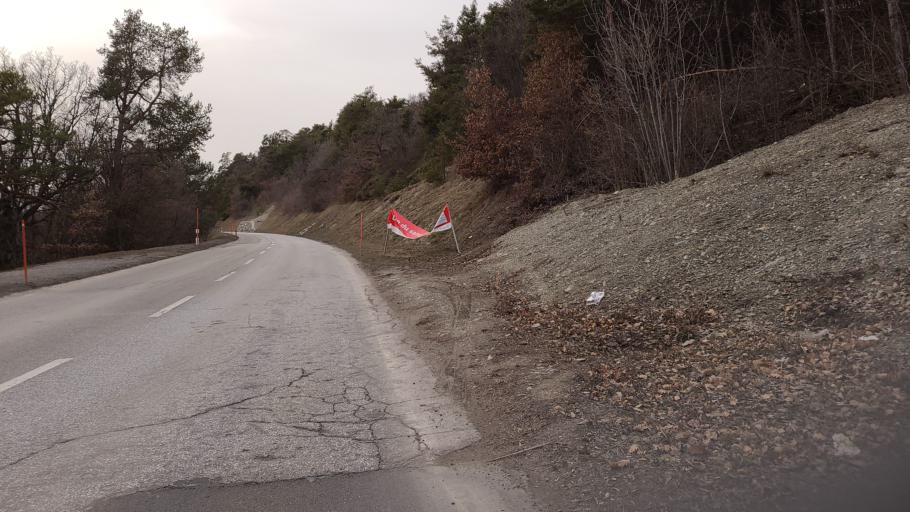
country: CH
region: Valais
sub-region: Sierre District
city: Chermignon-d'en Haut
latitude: 46.2835
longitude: 7.4642
